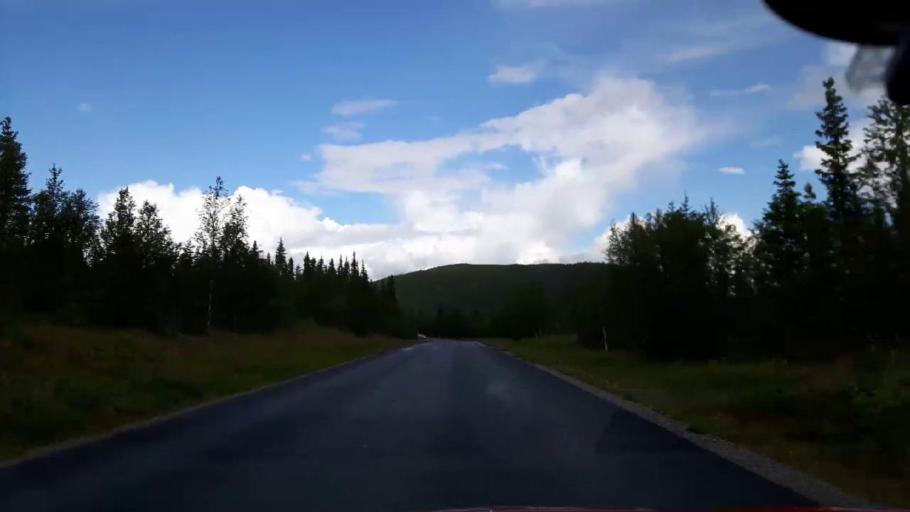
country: SE
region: Vaesterbotten
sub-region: Vilhelmina Kommun
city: Sjoberg
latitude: 65.0169
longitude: 15.1689
